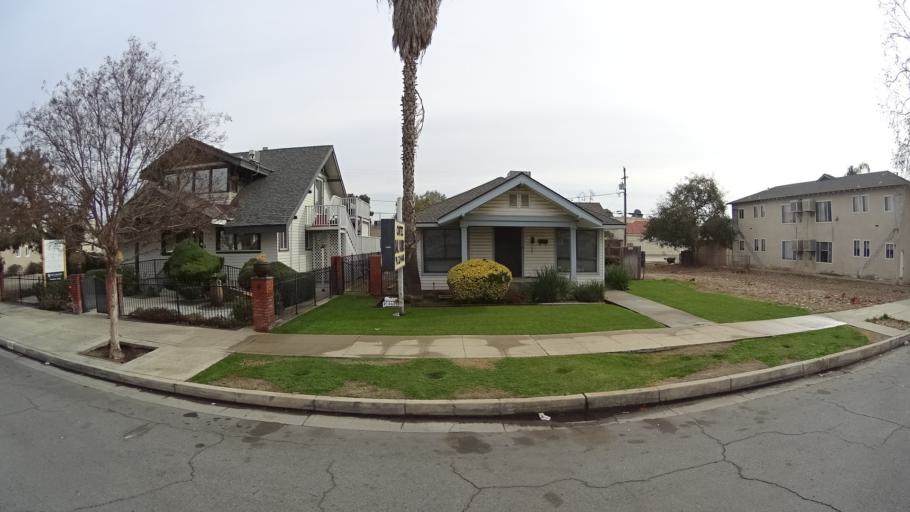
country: US
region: California
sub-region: Kern County
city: Bakersfield
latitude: 35.3696
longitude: -119.0176
